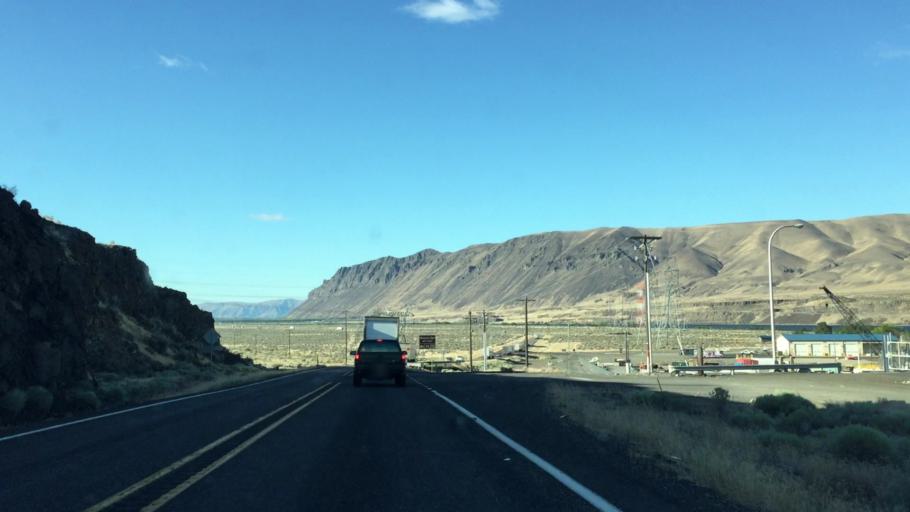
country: US
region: Washington
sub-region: Grant County
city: Mattawa
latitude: 46.8795
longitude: -119.9550
